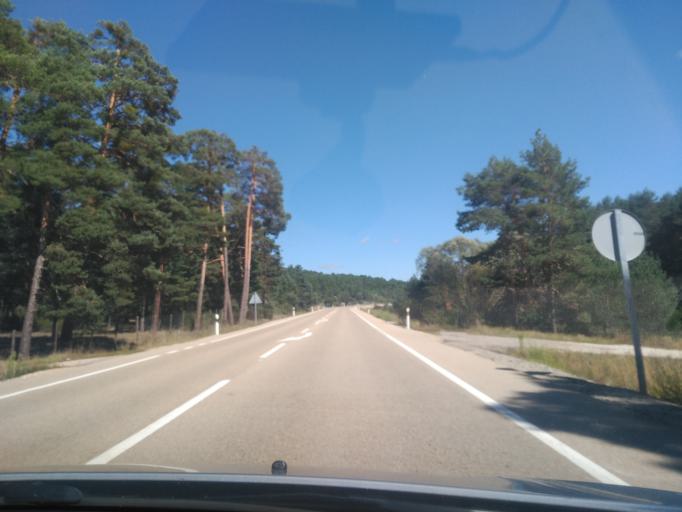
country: ES
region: Castille and Leon
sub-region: Provincia de Soria
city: Navaleno
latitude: 41.8396
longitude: -3.0276
